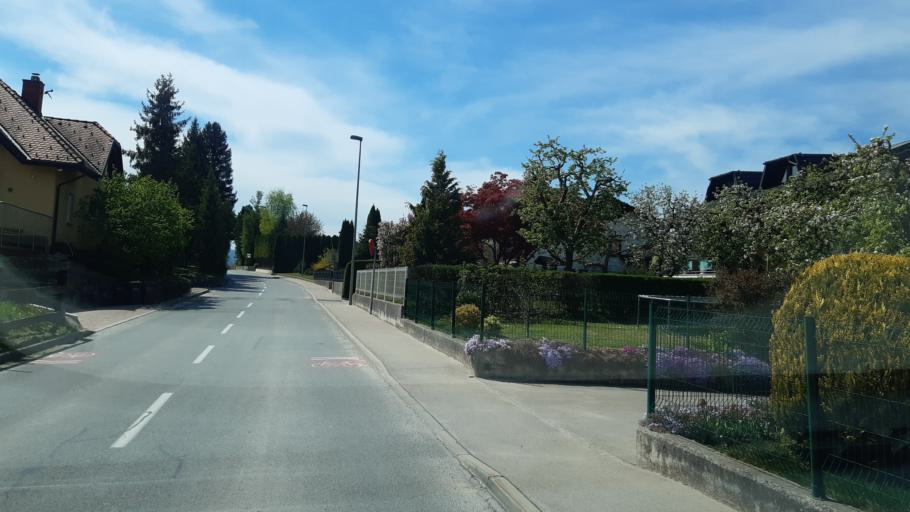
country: SI
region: Domzale
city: Radomlje
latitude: 46.1764
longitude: 14.6202
